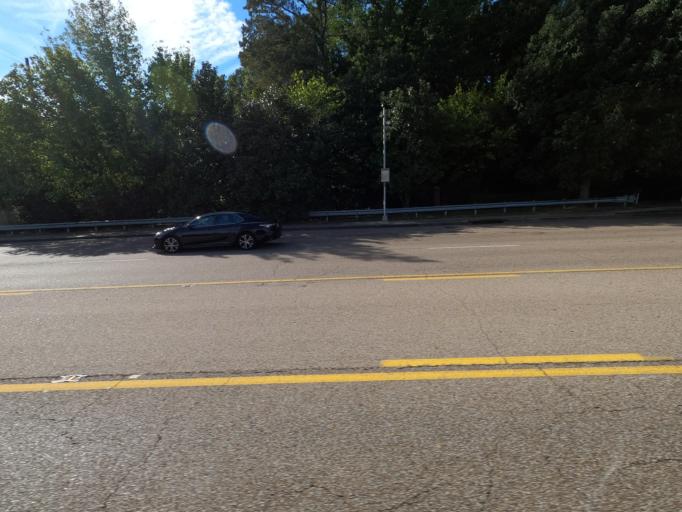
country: US
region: Tennessee
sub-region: Shelby County
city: Germantown
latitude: 35.0407
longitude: -89.7959
